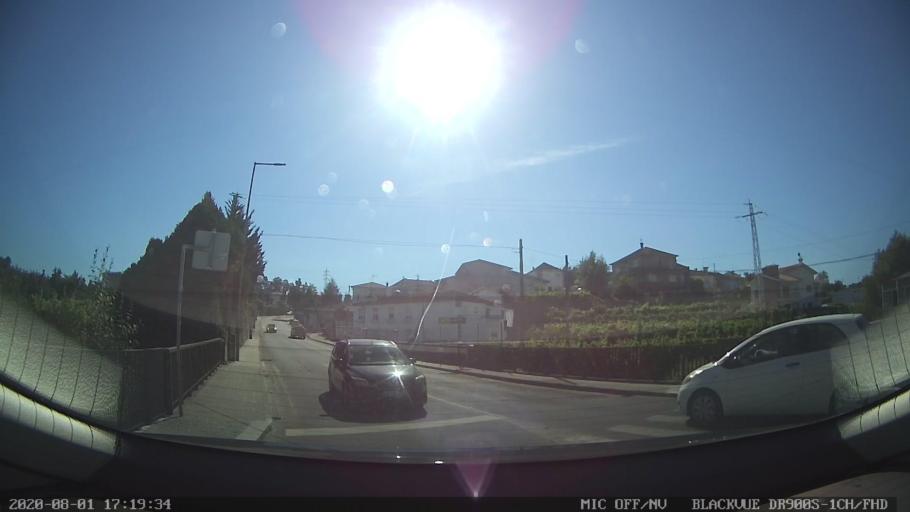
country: PT
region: Porto
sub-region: Santo Tirso
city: Santo Tirso
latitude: 41.3394
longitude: -8.4819
